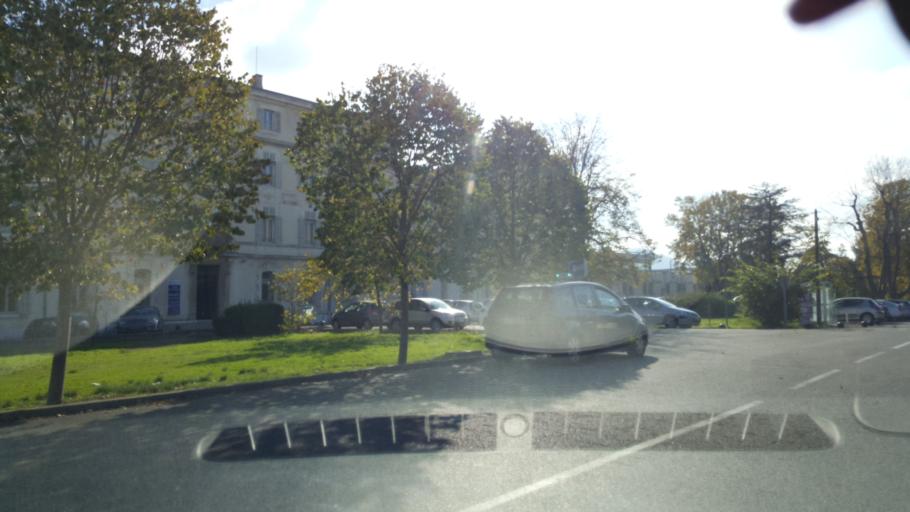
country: FR
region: Provence-Alpes-Cote d'Azur
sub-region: Departement des Bouches-du-Rhone
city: Marseille 09
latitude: 43.2607
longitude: 5.4104
